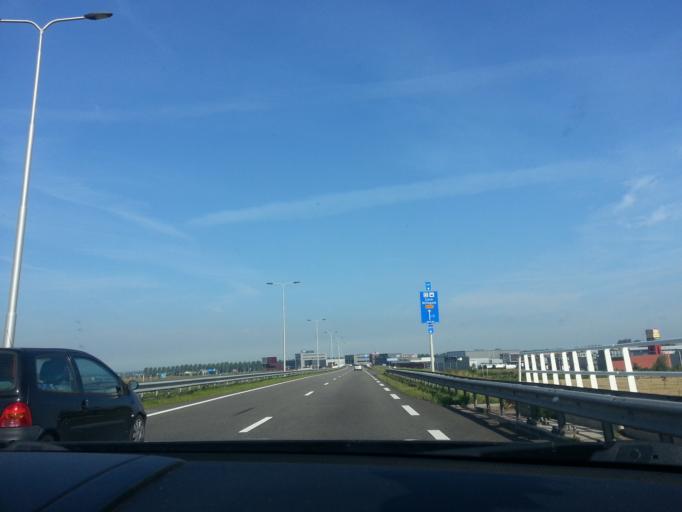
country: NL
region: South Holland
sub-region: Gemeente Kaag en Braassem
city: Oude Wetering
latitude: 52.2490
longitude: 4.6365
